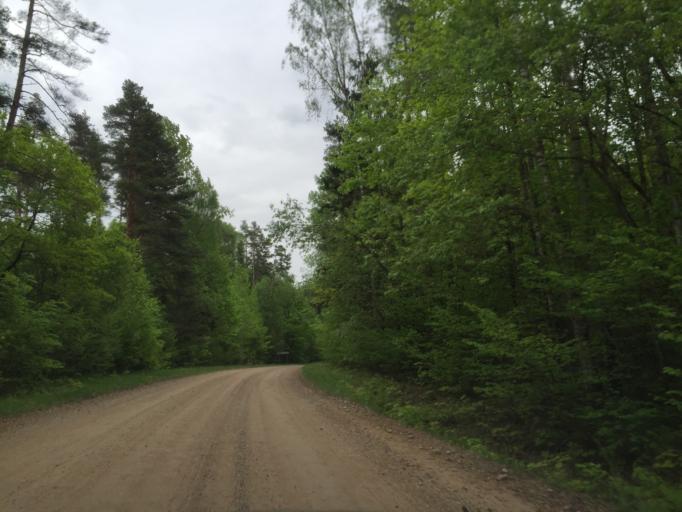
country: LV
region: Lielvarde
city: Lielvarde
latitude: 56.8056
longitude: 24.8195
